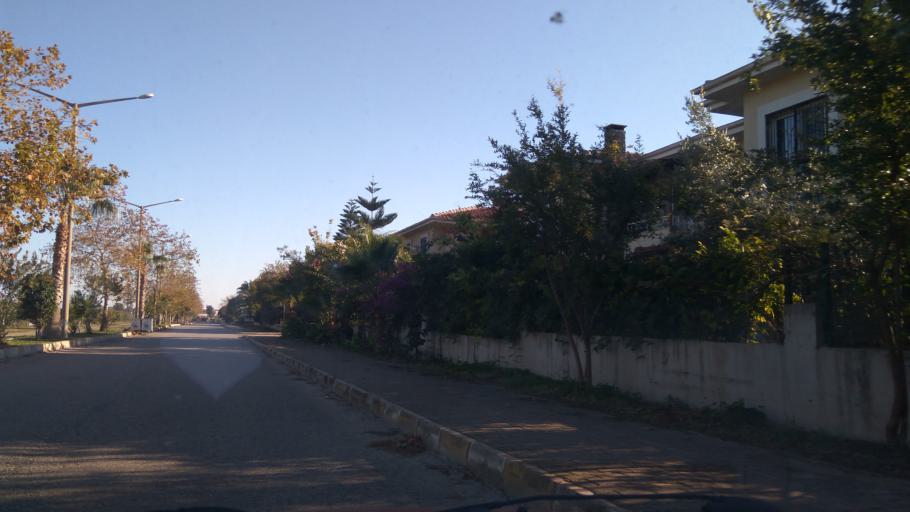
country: TR
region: Antalya
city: Kemer
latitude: 36.5703
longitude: 30.5584
